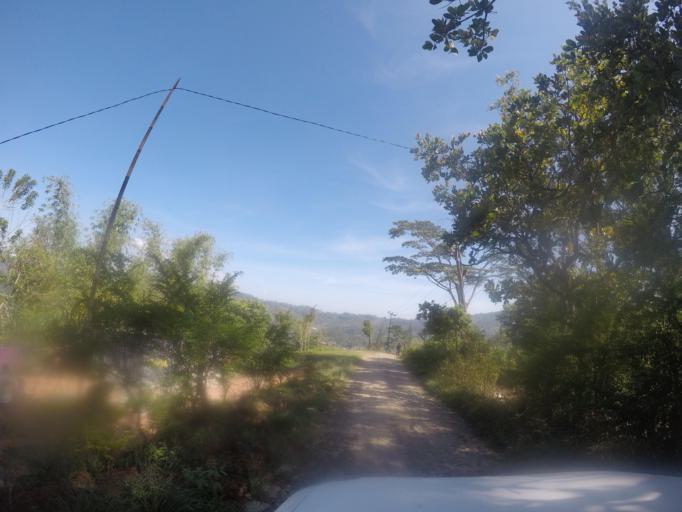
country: TL
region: Ermera
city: Gleno
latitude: -8.7286
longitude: 125.4375
